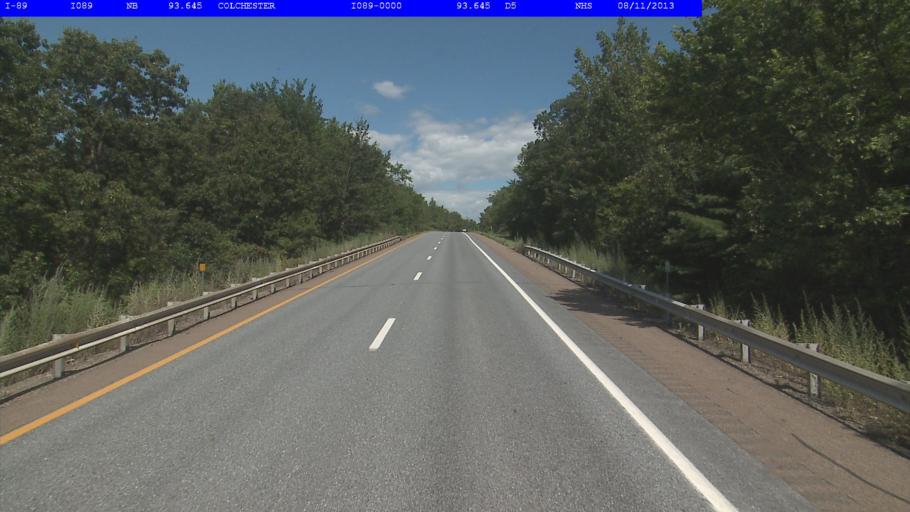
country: US
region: Vermont
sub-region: Chittenden County
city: Winooski
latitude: 44.5331
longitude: -73.1962
